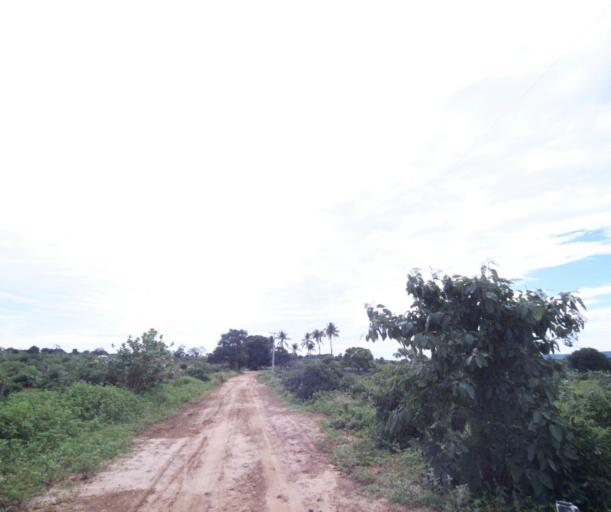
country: BR
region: Bahia
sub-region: Carinhanha
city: Carinhanha
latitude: -14.2401
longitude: -44.3940
